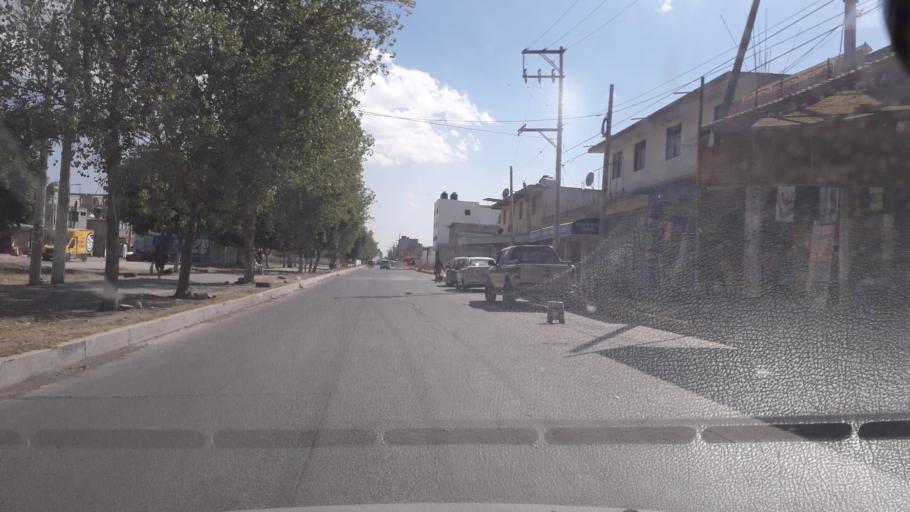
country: MX
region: Mexico
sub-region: Jaltenco
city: Alborada Jaltenco
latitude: 19.6542
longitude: -99.0668
